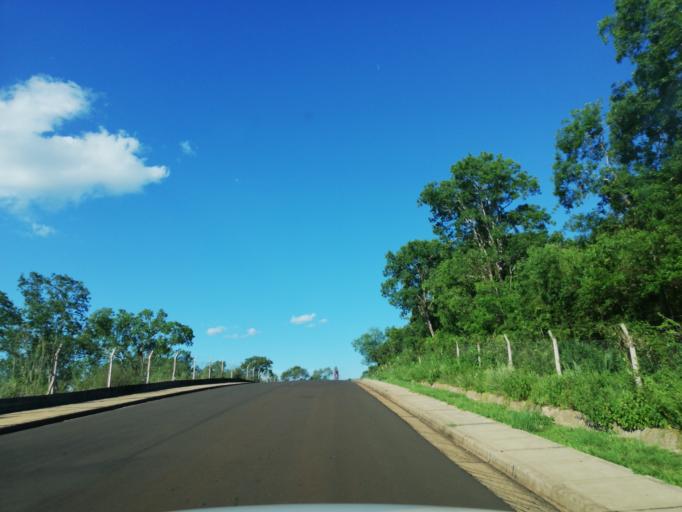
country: AR
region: Misiones
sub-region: Departamento de Candelaria
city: Candelaria
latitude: -27.4510
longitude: -55.7728
